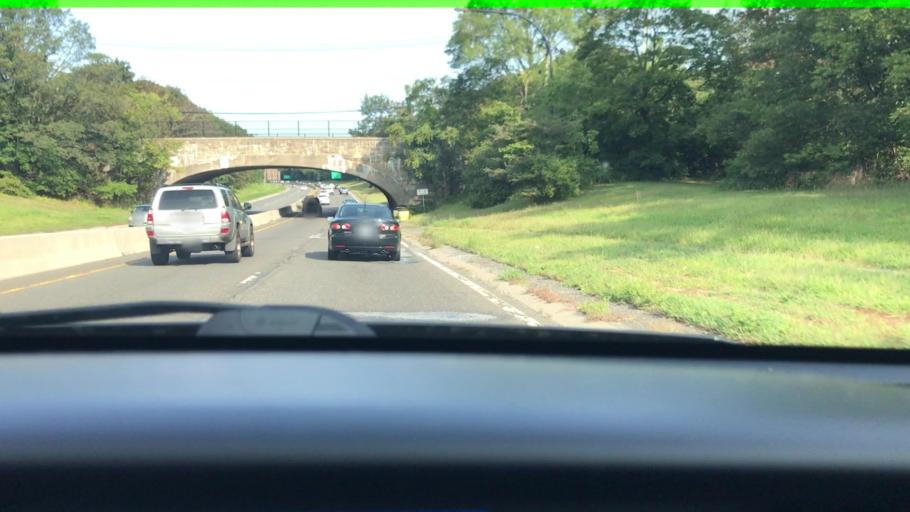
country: US
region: New York
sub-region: Nassau County
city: New Cassel
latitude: 40.7629
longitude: -73.5549
